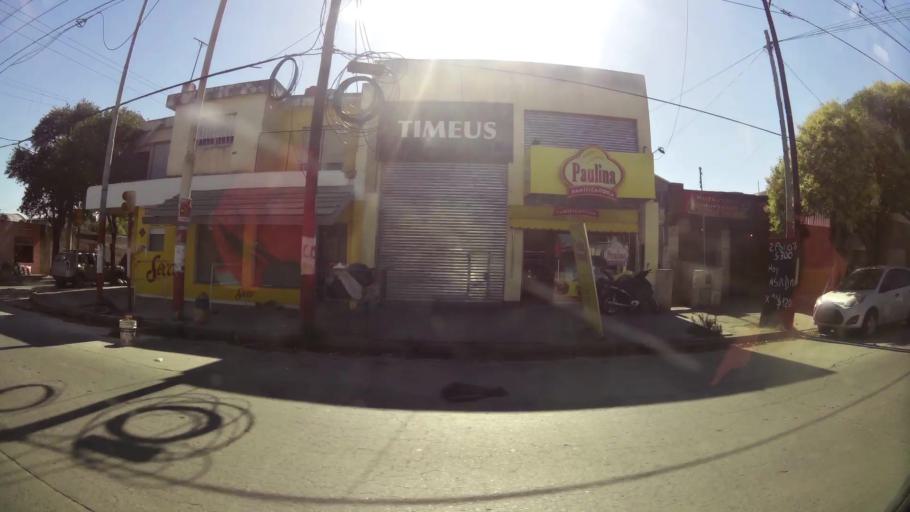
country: AR
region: Cordoba
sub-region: Departamento de Capital
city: Cordoba
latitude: -31.3722
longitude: -64.1839
